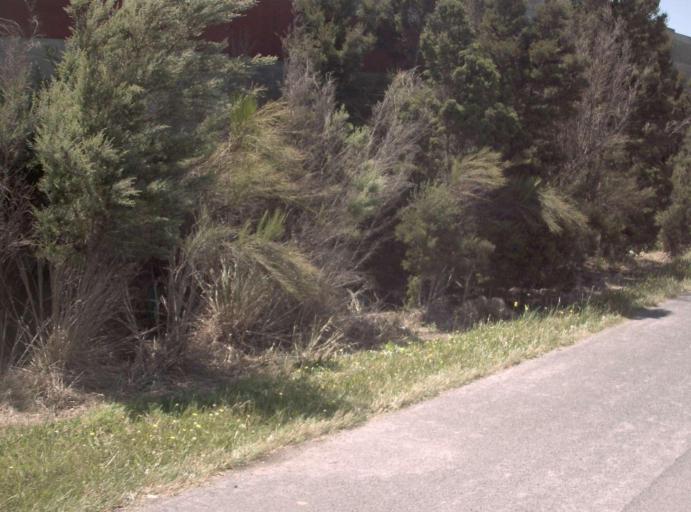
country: AU
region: Victoria
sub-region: Casey
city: Berwick
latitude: -38.0332
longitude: 145.3259
